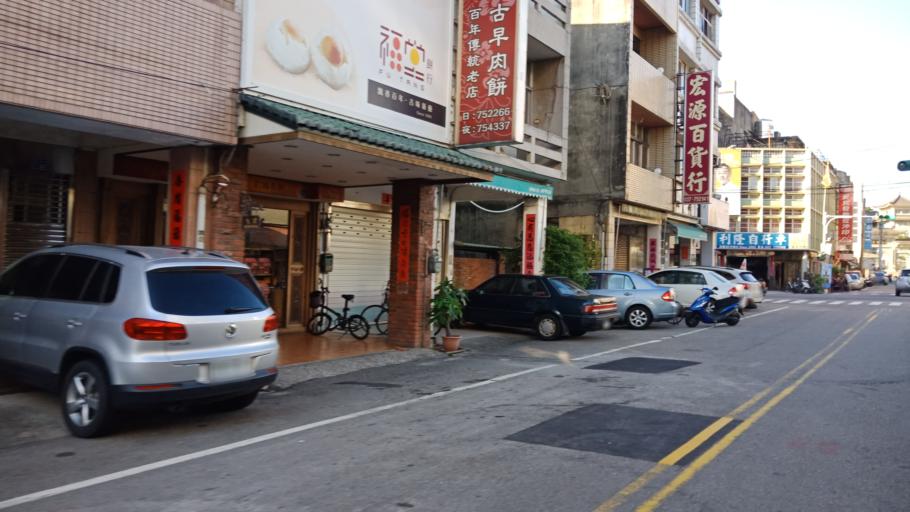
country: TW
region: Taiwan
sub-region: Miaoli
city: Miaoli
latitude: 24.4899
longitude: 120.6808
